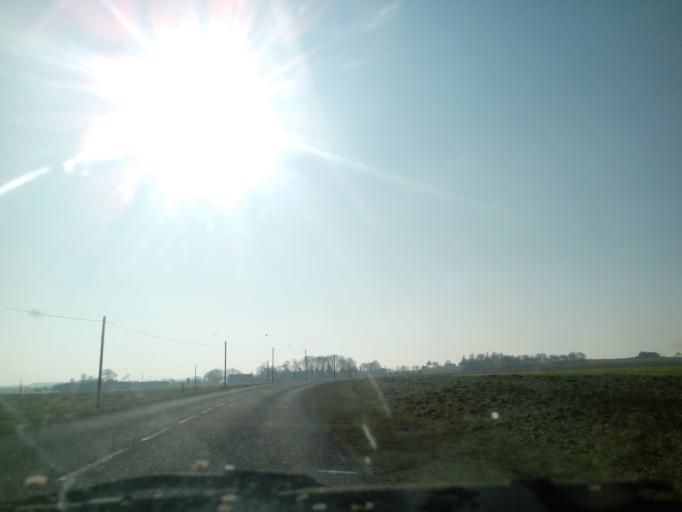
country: FR
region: Brittany
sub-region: Departement des Cotes-d'Armor
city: Merdrignac
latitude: 48.1688
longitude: -2.4362
